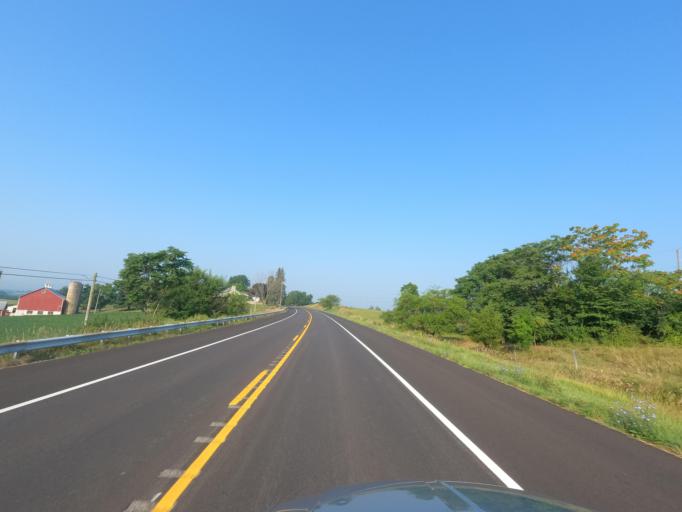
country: US
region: Pennsylvania
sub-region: Franklin County
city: Waynesboro
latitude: 39.7059
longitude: -77.5931
